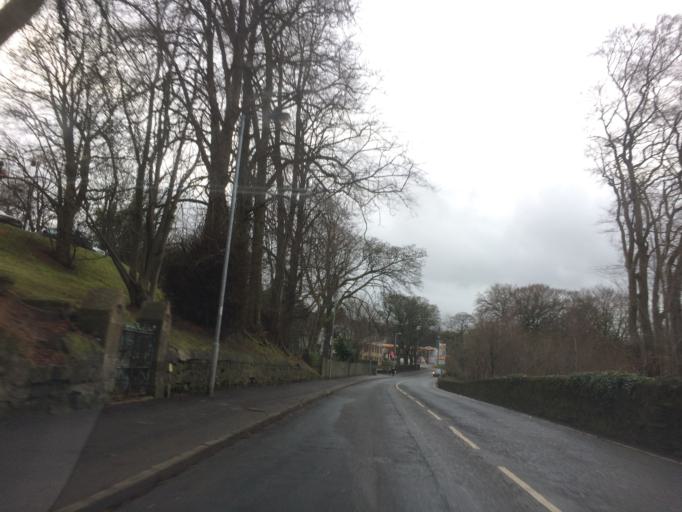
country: GB
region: Scotland
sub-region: East Renfrewshire
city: Giffnock
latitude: 55.8035
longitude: -4.3197
